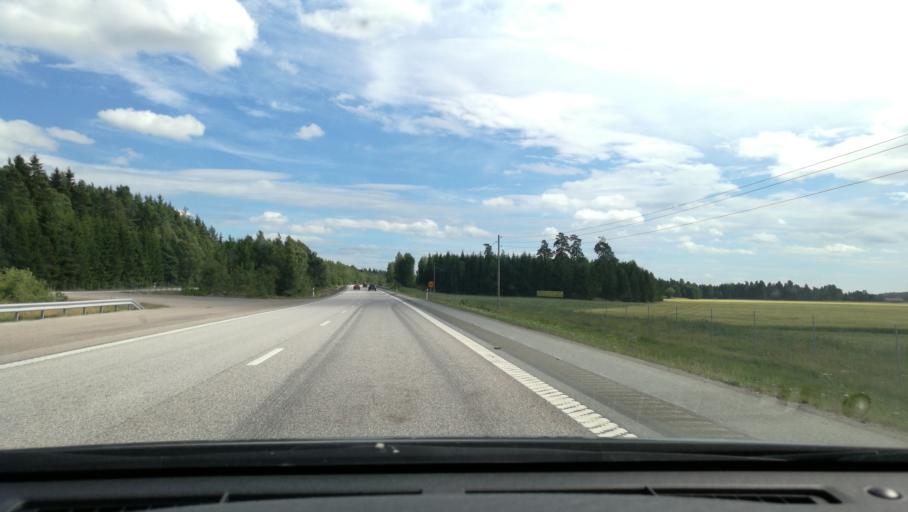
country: SE
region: Uppsala
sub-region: Habo Kommun
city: Balsta
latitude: 59.5557
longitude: 17.5822
